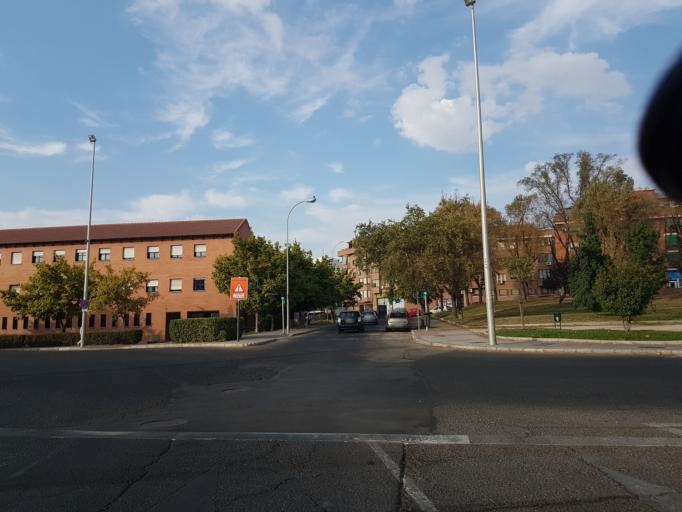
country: ES
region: Madrid
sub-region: Provincia de Madrid
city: Moratalaz
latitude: 40.4271
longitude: -3.6471
